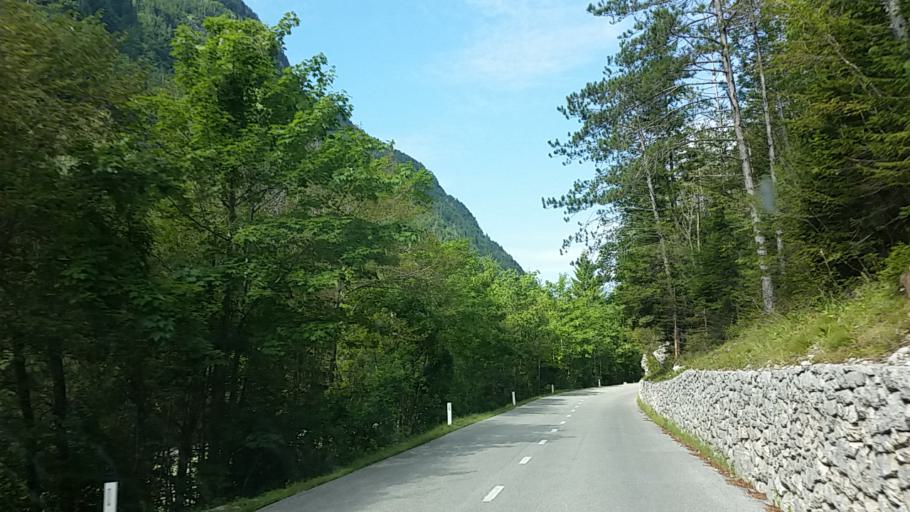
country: SI
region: Bovec
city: Bovec
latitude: 46.3375
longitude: 13.6273
